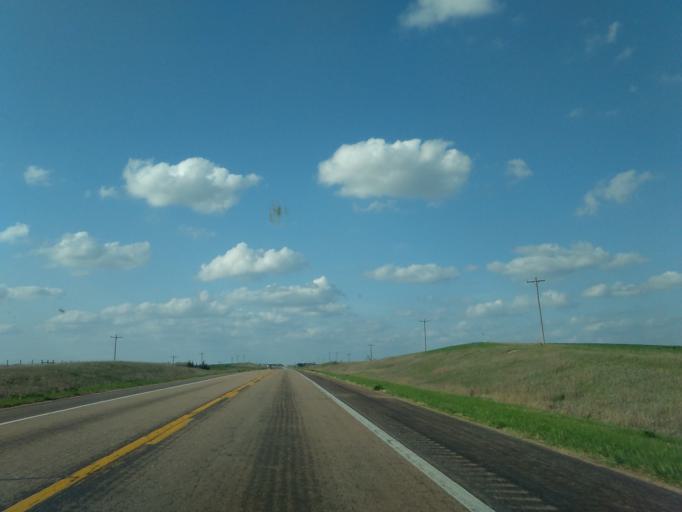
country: US
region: Nebraska
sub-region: Webster County
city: Red Cloud
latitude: 40.1208
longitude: -98.5189
